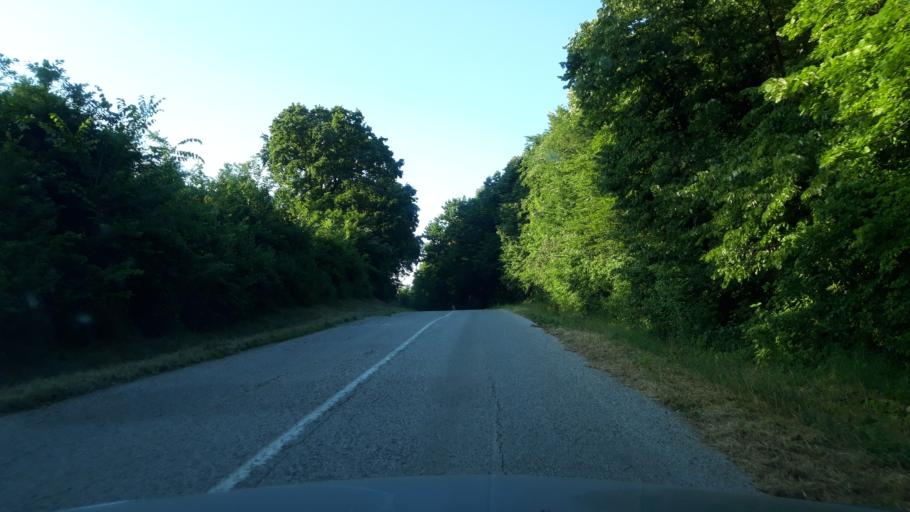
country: RS
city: Glozan
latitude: 45.1474
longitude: 19.5791
